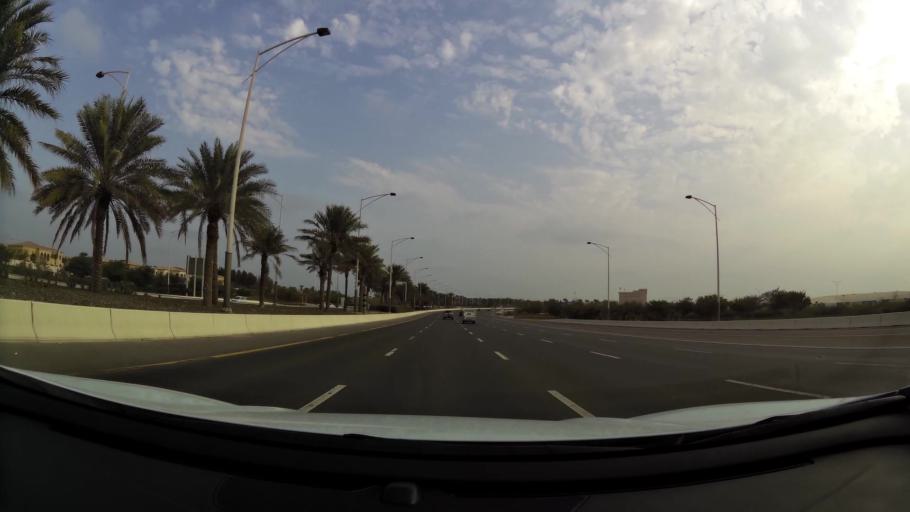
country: AE
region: Abu Dhabi
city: Abu Dhabi
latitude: 24.5364
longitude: 54.4358
